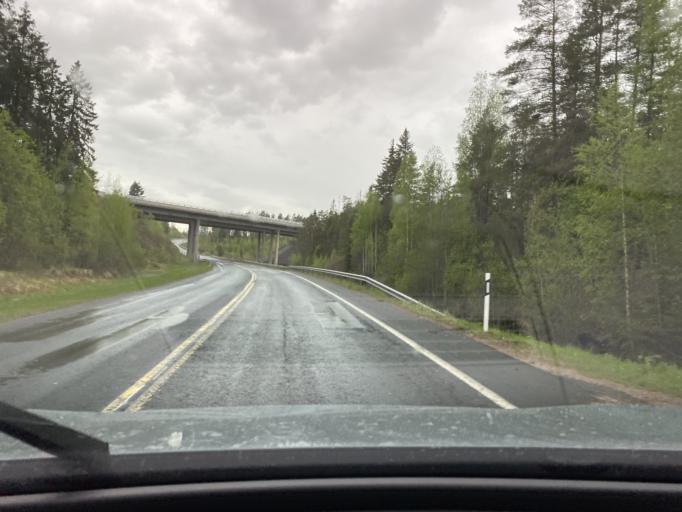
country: FI
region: Varsinais-Suomi
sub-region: Salo
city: Suomusjaervi
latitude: 60.3721
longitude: 23.6532
